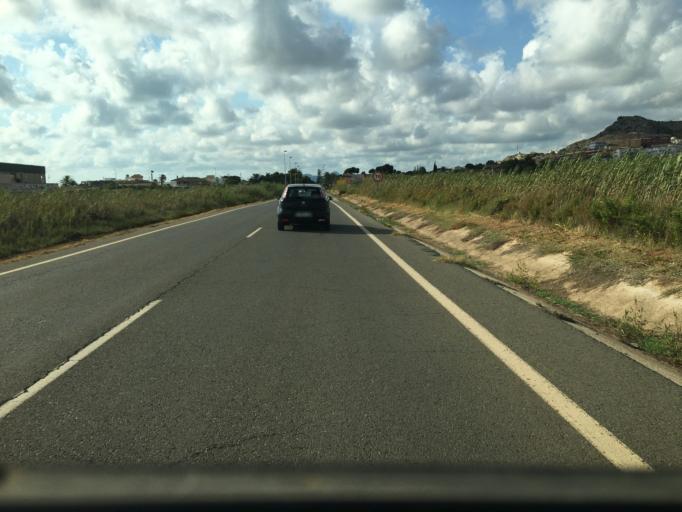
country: ES
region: Murcia
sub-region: Murcia
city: Los Alcazares
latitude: 37.6979
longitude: -0.8441
